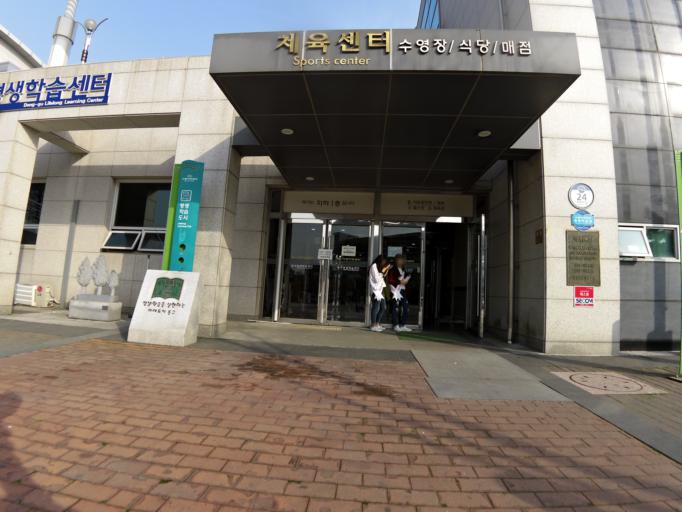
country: KR
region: Daegu
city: Daegu
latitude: 35.8798
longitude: 128.6514
